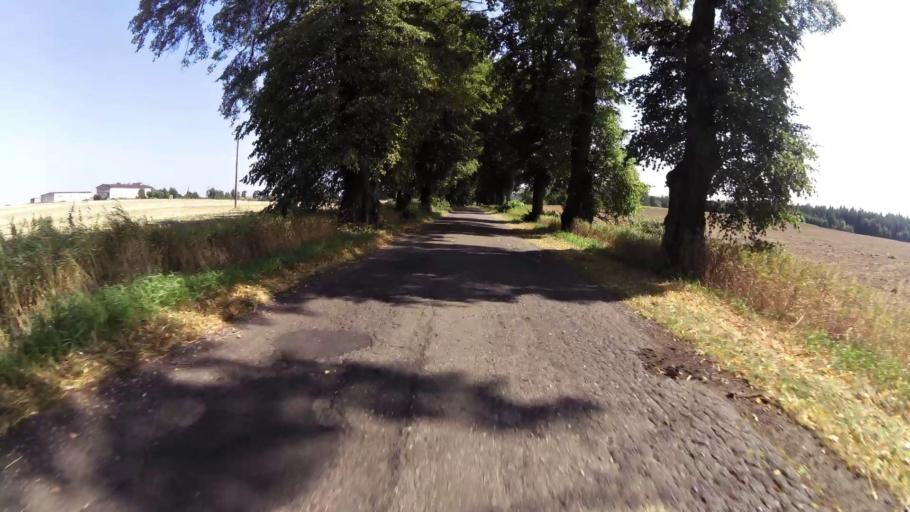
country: PL
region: Greater Poland Voivodeship
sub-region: Powiat pilski
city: Szydlowo
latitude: 53.1998
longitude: 16.5250
